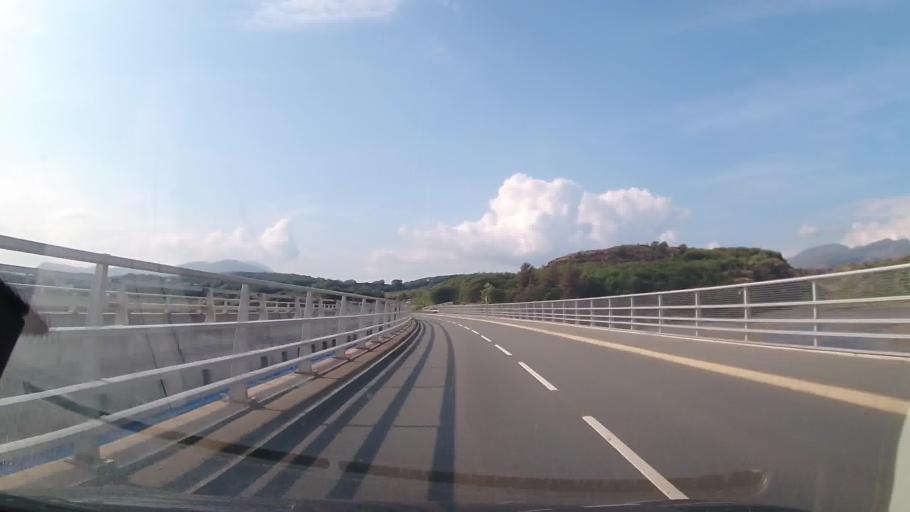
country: GB
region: Wales
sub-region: Gwynedd
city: Penrhyndeudraeth
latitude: 52.9245
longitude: -4.0556
